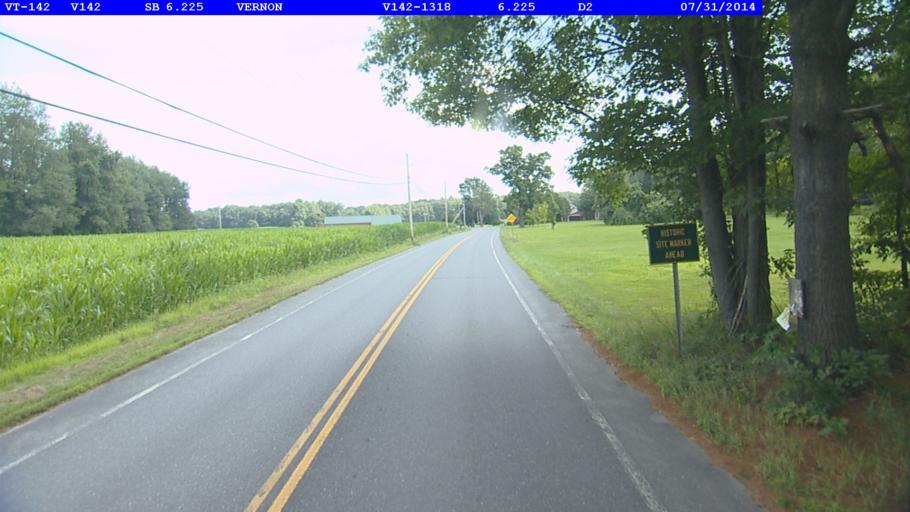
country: US
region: New Hampshire
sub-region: Cheshire County
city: Hinsdale
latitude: 42.7914
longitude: -72.5339
